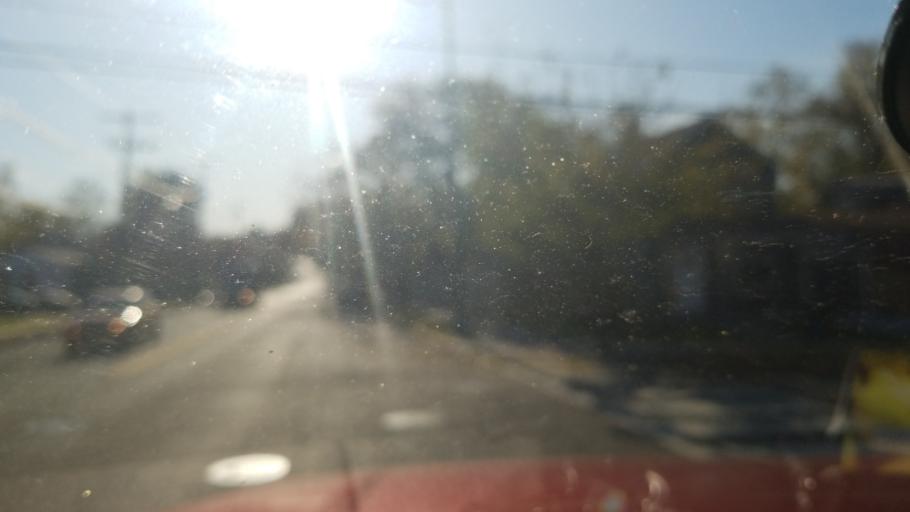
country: US
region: Maryland
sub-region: Prince George's County
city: Fairmount Heights
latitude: 38.9012
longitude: -76.9201
